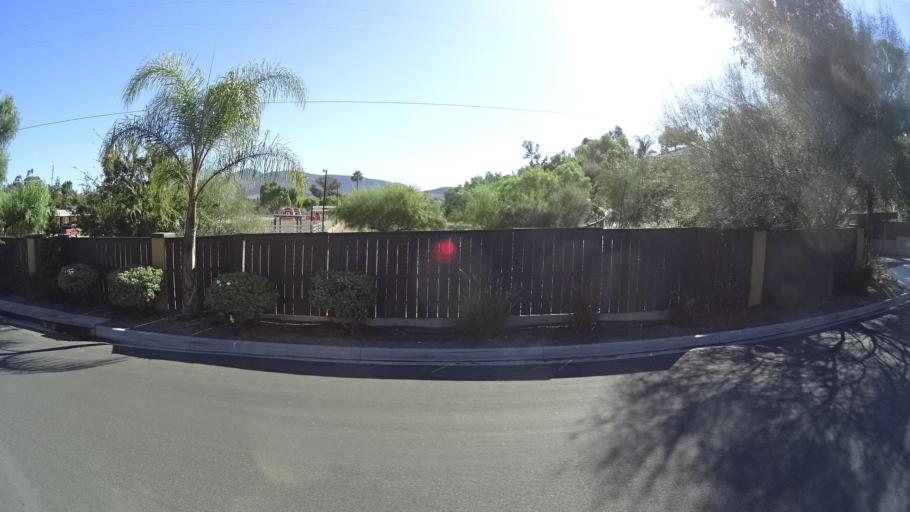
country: US
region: California
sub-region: San Diego County
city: Bonita
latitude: 32.6761
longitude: -117.0076
